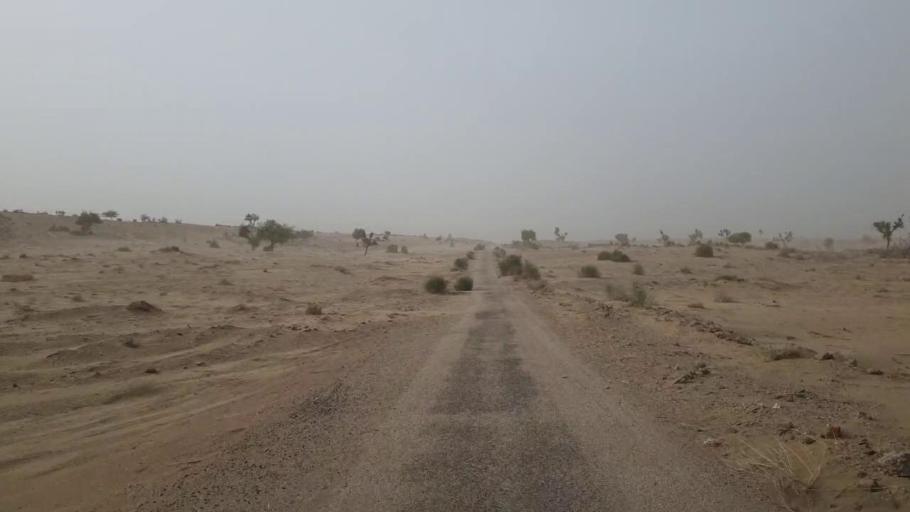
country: PK
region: Sindh
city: Islamkot
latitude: 24.5631
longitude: 70.3626
